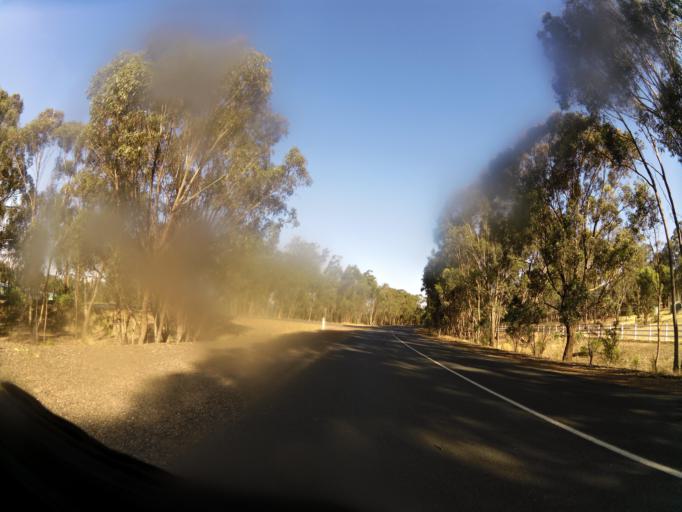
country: AU
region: Victoria
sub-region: Murrindindi
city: Kinglake West
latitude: -37.0035
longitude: 145.1191
